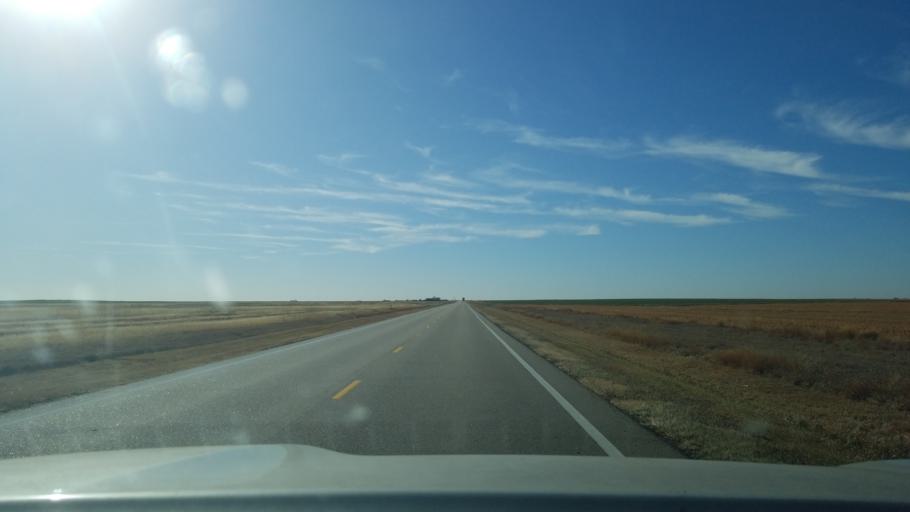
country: US
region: Kansas
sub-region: Ness County
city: Ness City
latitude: 38.3461
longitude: -99.8978
